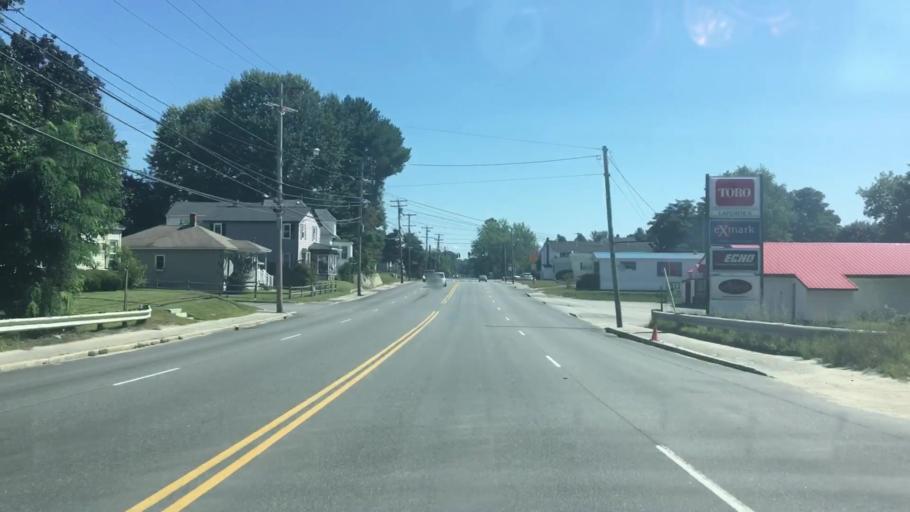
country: US
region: Maine
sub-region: Androscoggin County
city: Lewiston
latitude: 44.1018
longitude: -70.1635
